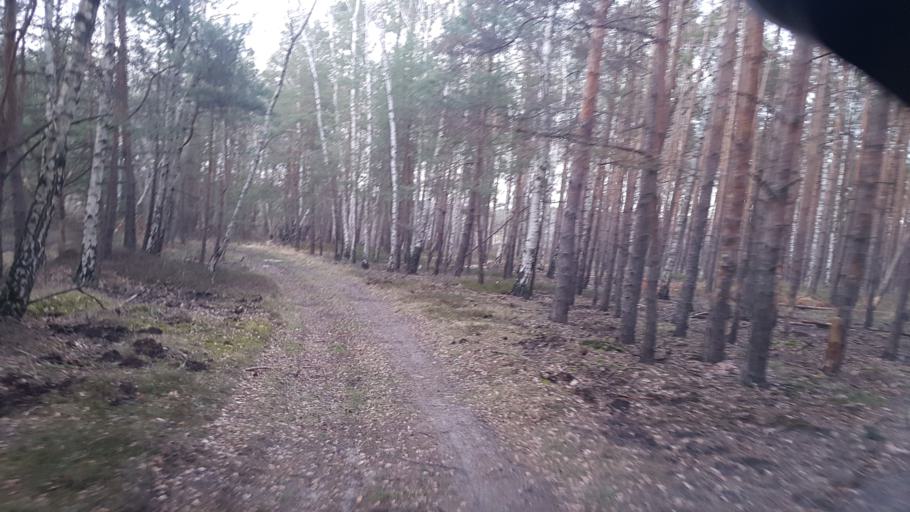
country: DE
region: Brandenburg
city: Schonborn
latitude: 51.5955
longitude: 13.4706
